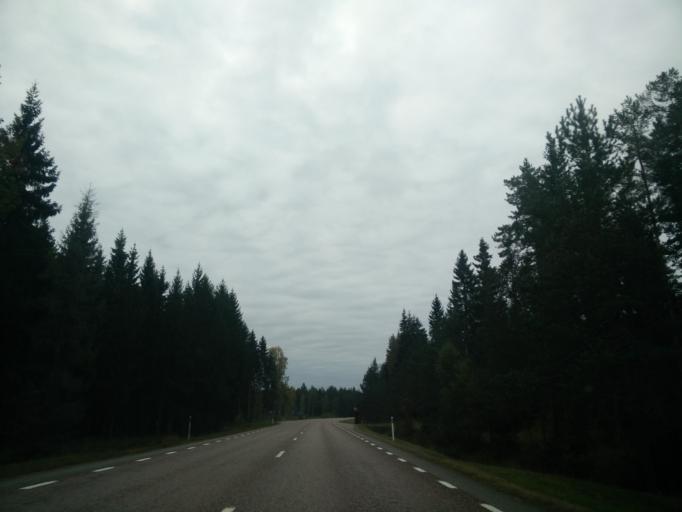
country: SE
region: Gaevleborg
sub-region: Gavle Kommun
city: Norrsundet
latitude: 60.8511
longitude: 17.1933
